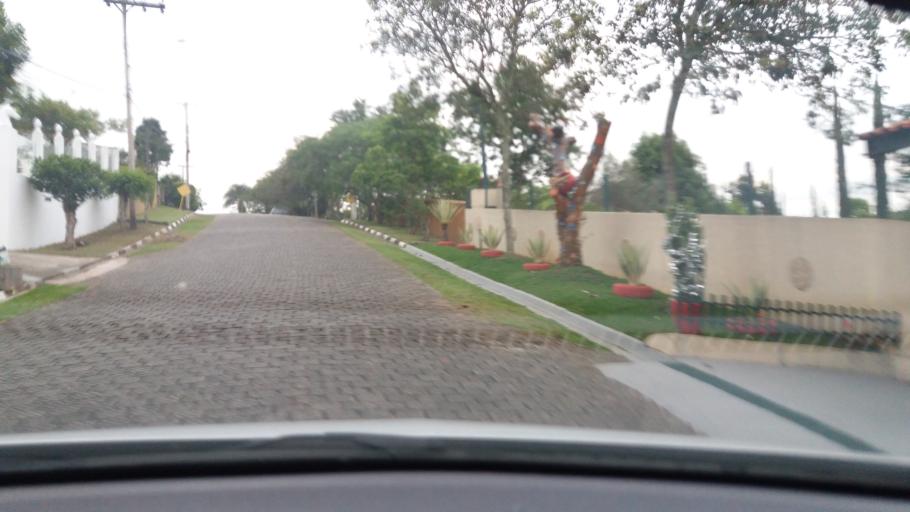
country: BR
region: Sao Paulo
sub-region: Bom Jesus Dos Perdoes
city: Bom Jesus dos Perdoes
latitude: -23.1672
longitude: -46.4528
